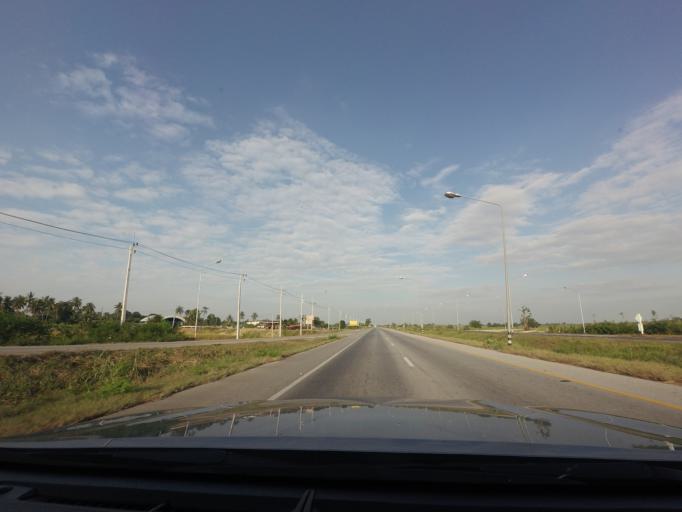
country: TH
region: Nakhon Sawan
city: Nakhon Sawan
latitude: 15.7576
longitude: 100.0921
